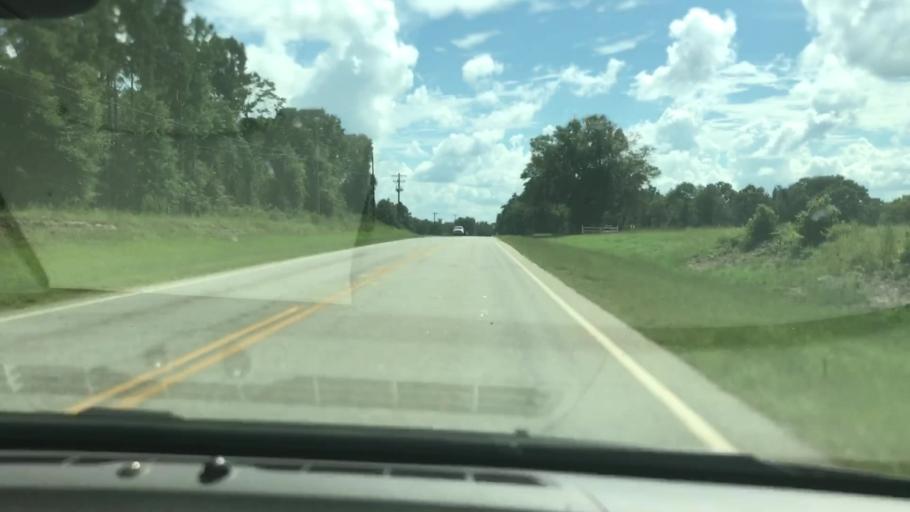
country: US
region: Georgia
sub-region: Clay County
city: Fort Gaines
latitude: 31.7011
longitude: -85.0427
